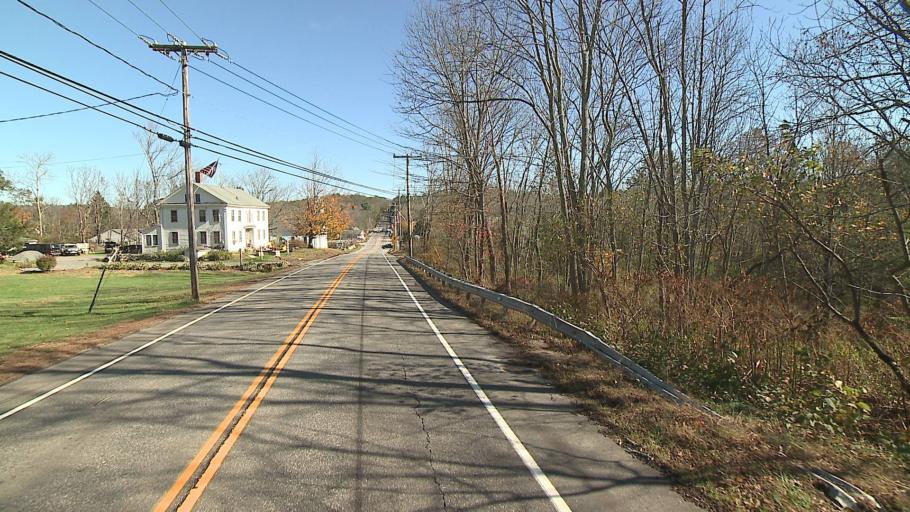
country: US
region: Connecticut
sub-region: Tolland County
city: Storrs
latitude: 41.8626
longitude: -72.1650
